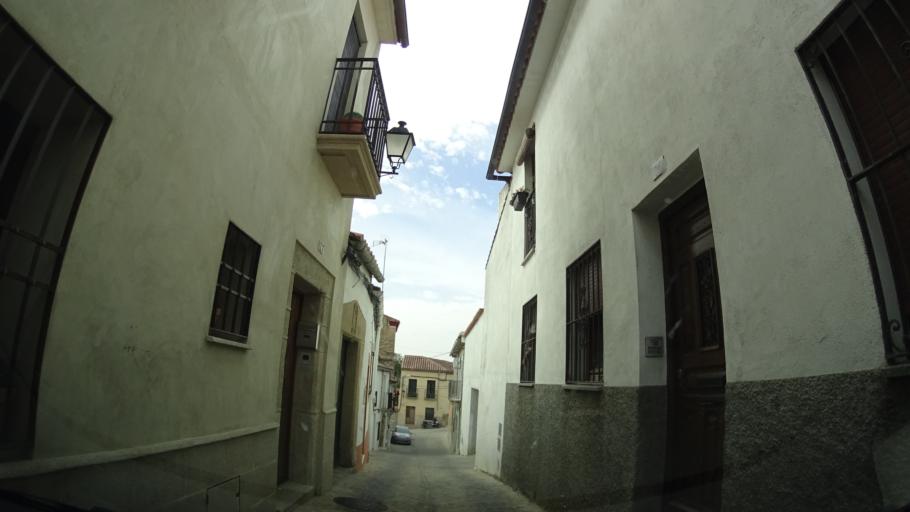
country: ES
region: Extremadura
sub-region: Provincia de Caceres
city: Trujillo
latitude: 39.4586
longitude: -5.8831
